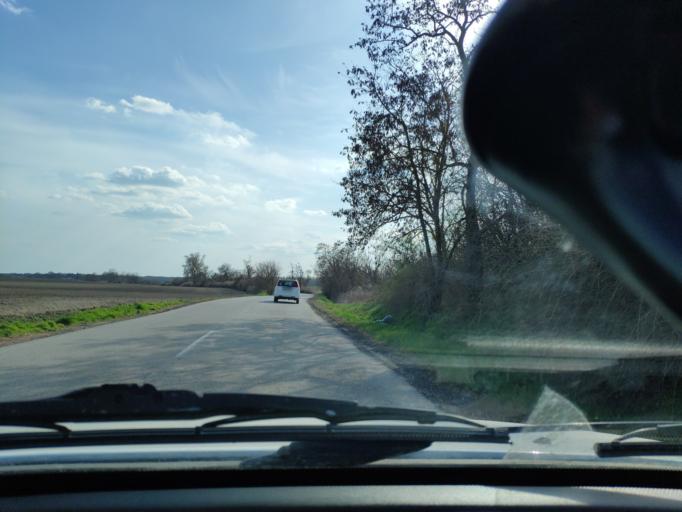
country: HU
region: Fejer
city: Adony
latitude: 47.1320
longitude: 18.8986
